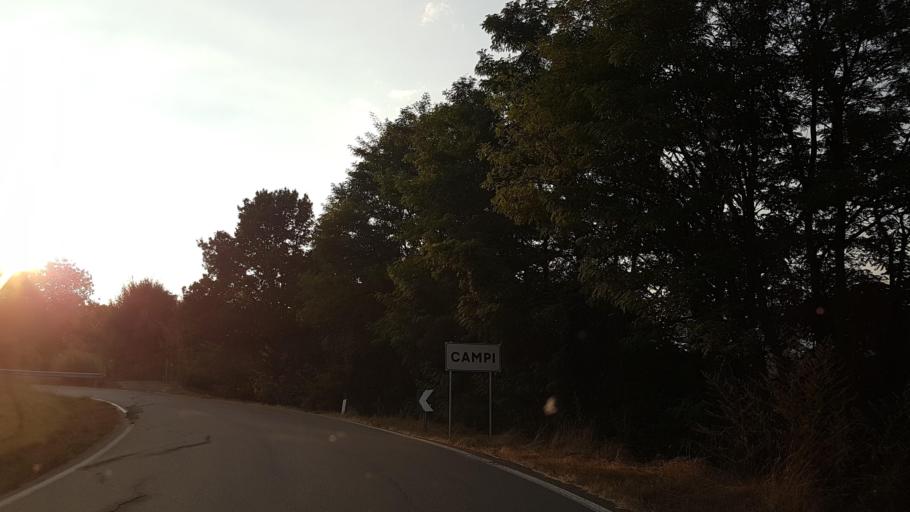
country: IT
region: Emilia-Romagna
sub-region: Provincia di Parma
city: Albareto
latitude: 44.4757
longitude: 9.7076
